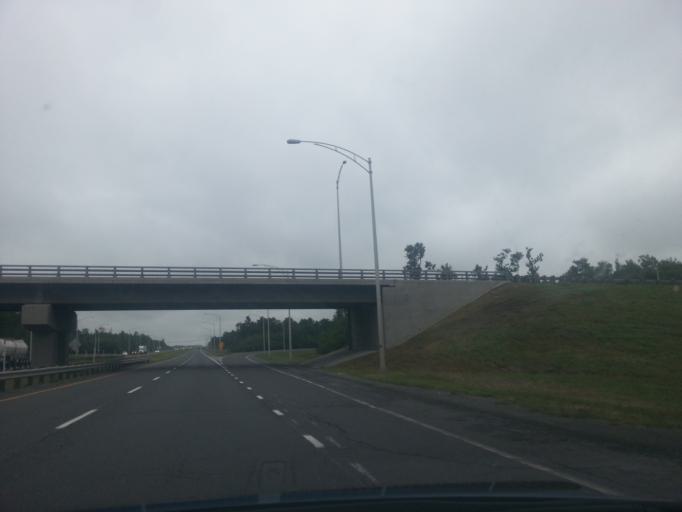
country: CA
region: Quebec
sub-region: Centre-du-Quebec
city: Drummondville
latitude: 45.9091
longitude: -72.4928
